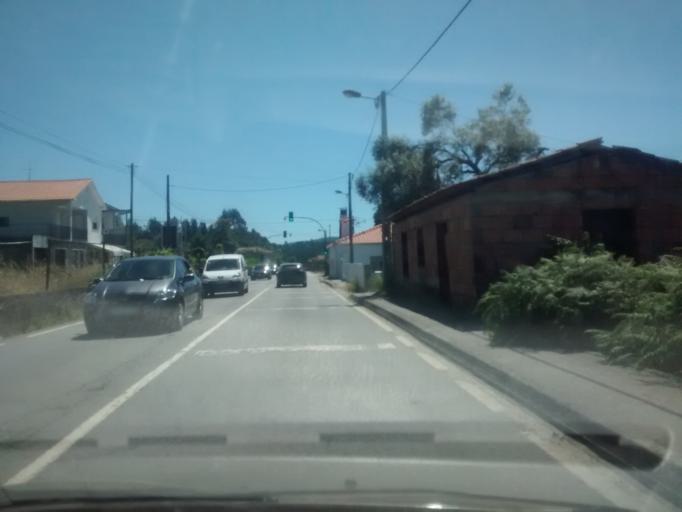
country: PT
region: Braga
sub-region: Barcelos
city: Galegos
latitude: 41.5268
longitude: -8.5630
